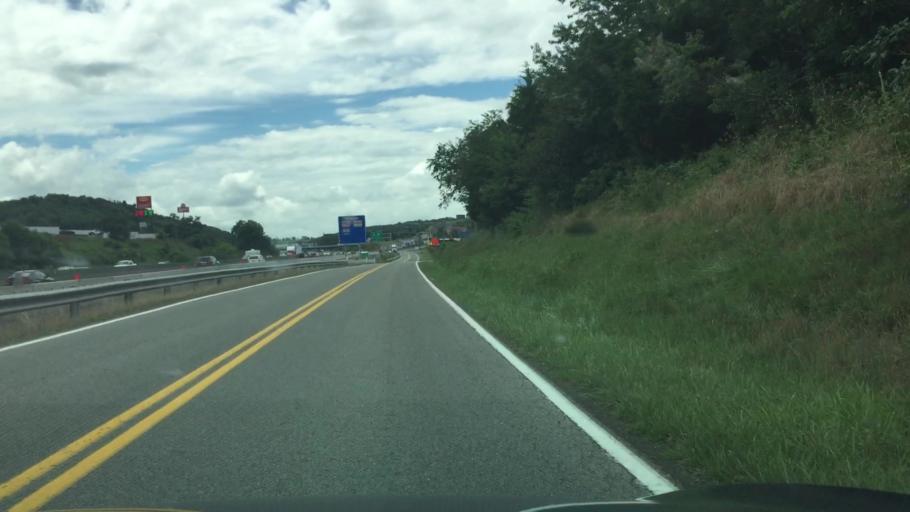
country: US
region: Virginia
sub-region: Wythe County
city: Wytheville
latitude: 36.9469
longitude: -80.9402
